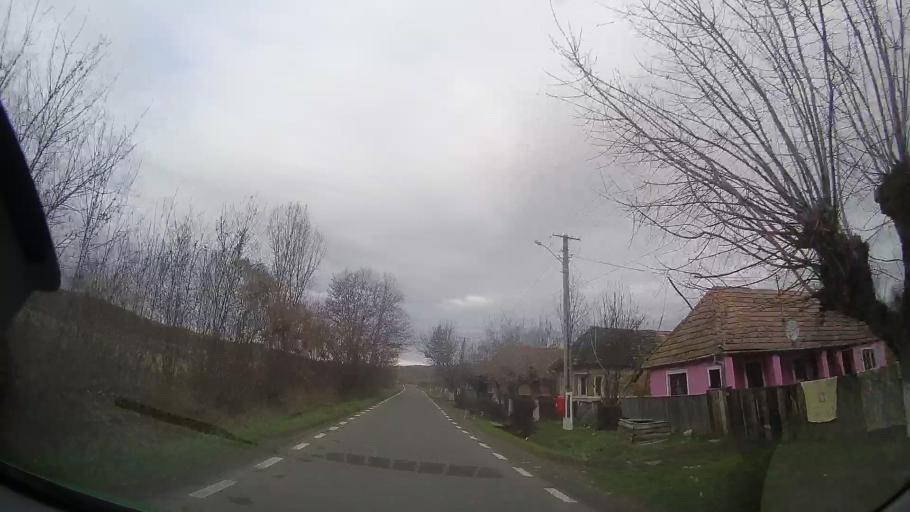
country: RO
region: Mures
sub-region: Comuna Cozma
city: Cozma
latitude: 46.7860
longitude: 24.5485
